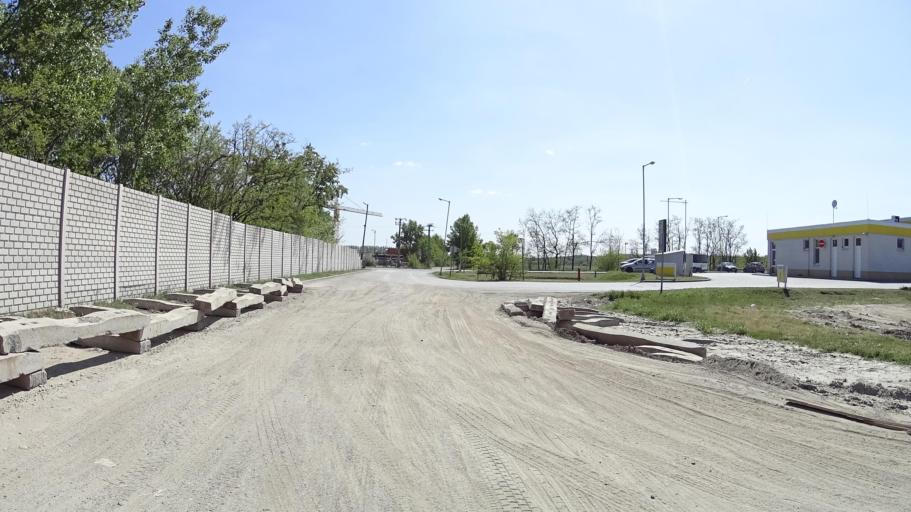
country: HU
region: Pest
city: Gyal
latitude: 47.3591
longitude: 19.2007
